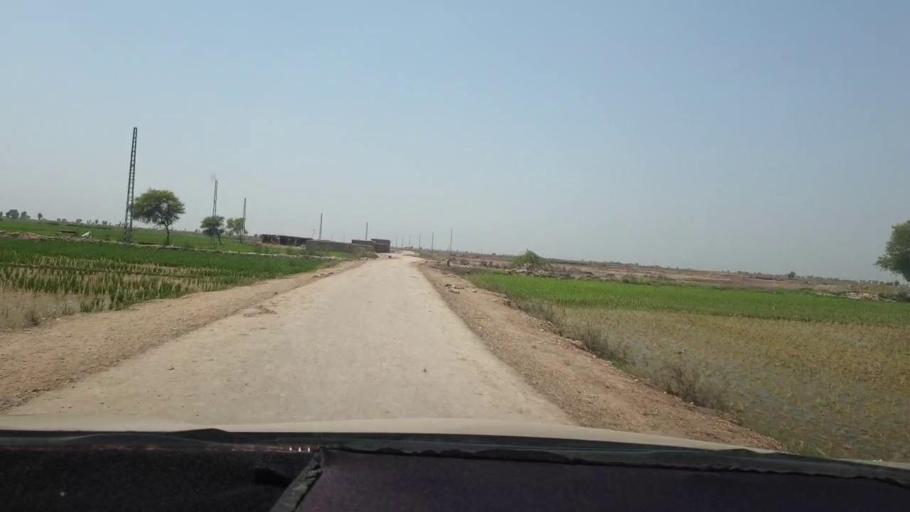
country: PK
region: Sindh
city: Shahdadkot
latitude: 27.8340
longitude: 67.8882
